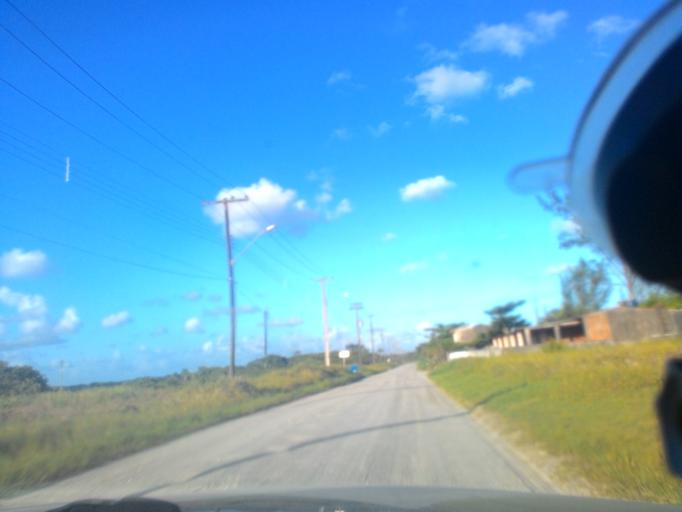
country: BR
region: Sao Paulo
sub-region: Cananeia
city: Cananeia
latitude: -24.8897
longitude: -47.7484
